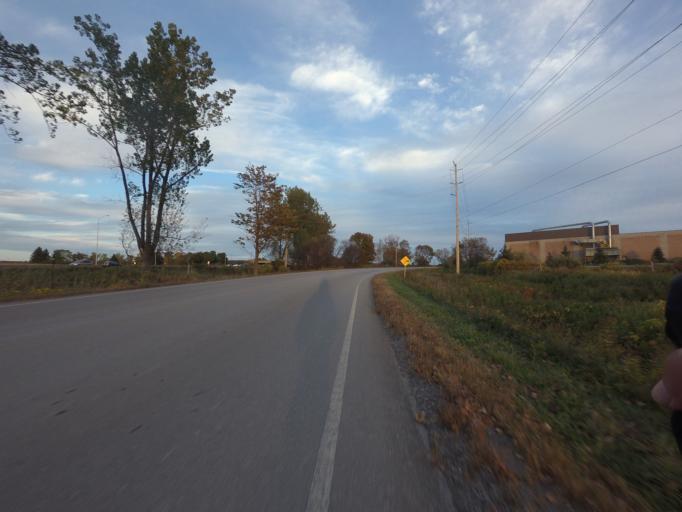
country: CA
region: Ontario
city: Oshawa
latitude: 43.9008
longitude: -78.6471
